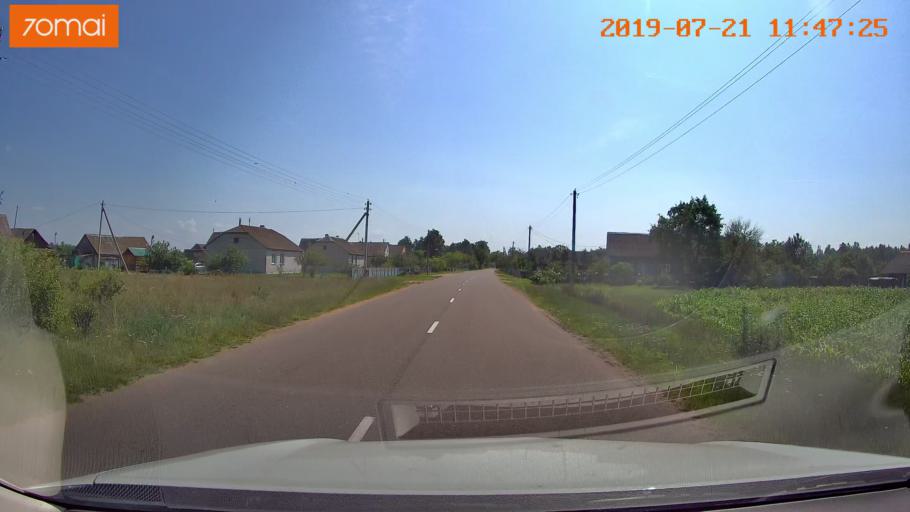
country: BY
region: Grodnenskaya
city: Lyubcha
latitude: 53.9027
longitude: 26.0472
